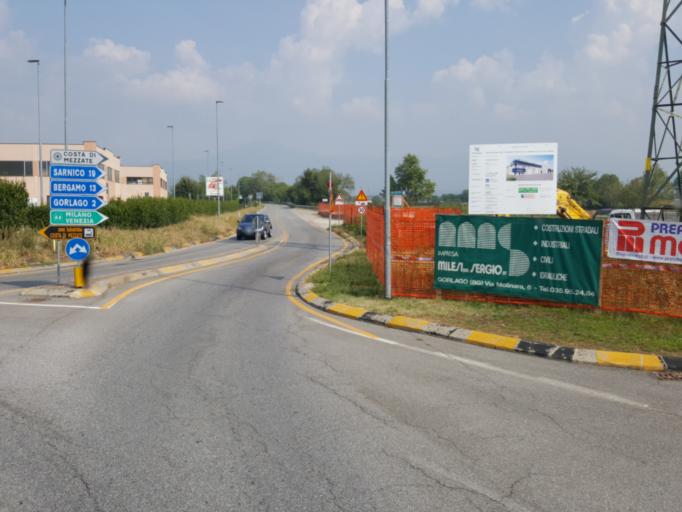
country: IT
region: Lombardy
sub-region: Provincia di Bergamo
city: Bolgare
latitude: 45.6481
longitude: 9.8078
